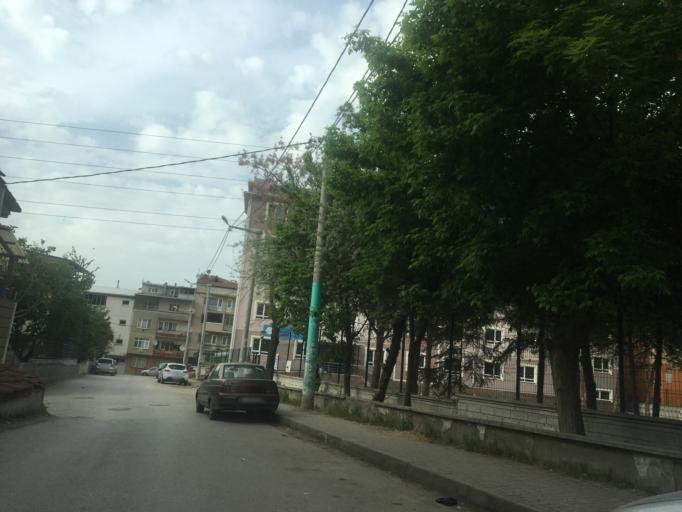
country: TR
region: Bursa
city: Yildirim
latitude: 40.2038
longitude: 29.0463
